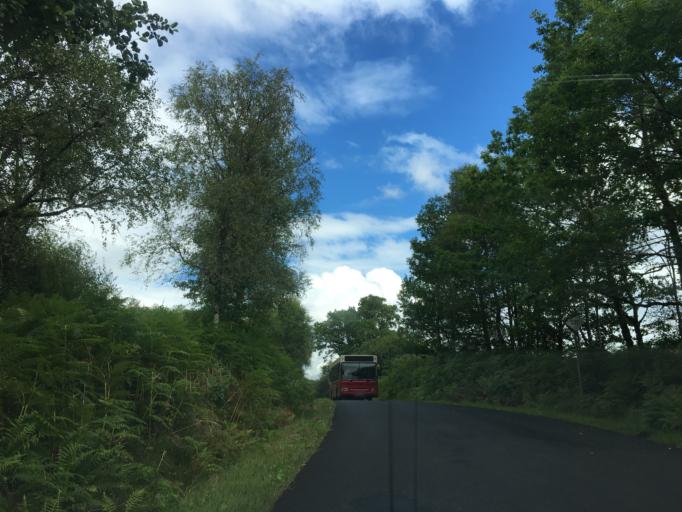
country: GB
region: Scotland
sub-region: Argyll and Bute
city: Oban
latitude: 56.3178
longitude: -5.2277
